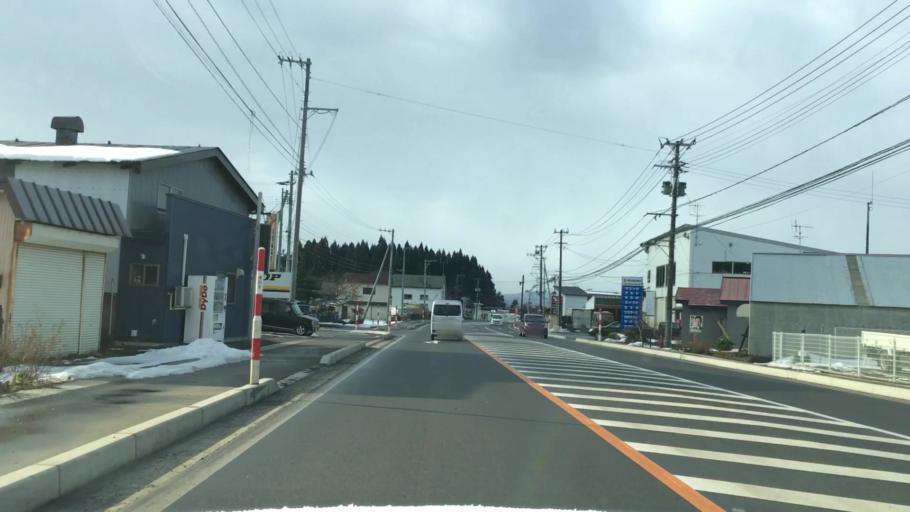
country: JP
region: Akita
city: Odate
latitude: 40.3091
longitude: 140.5693
